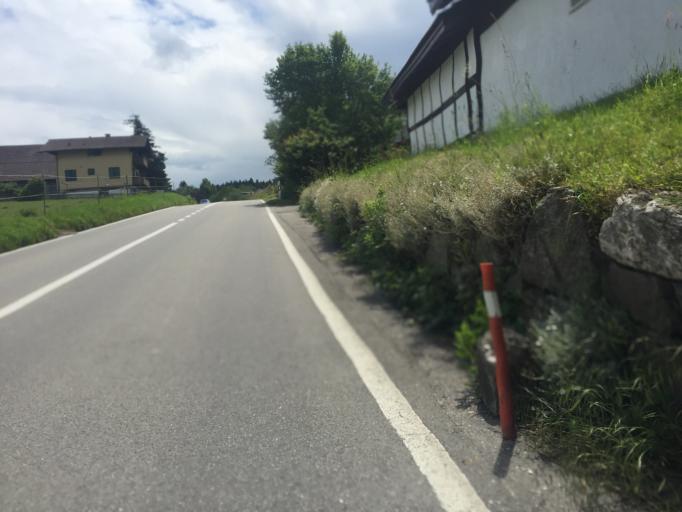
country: CH
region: Bern
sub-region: Bern-Mittelland District
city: Kirchlindach
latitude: 46.9887
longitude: 7.4073
